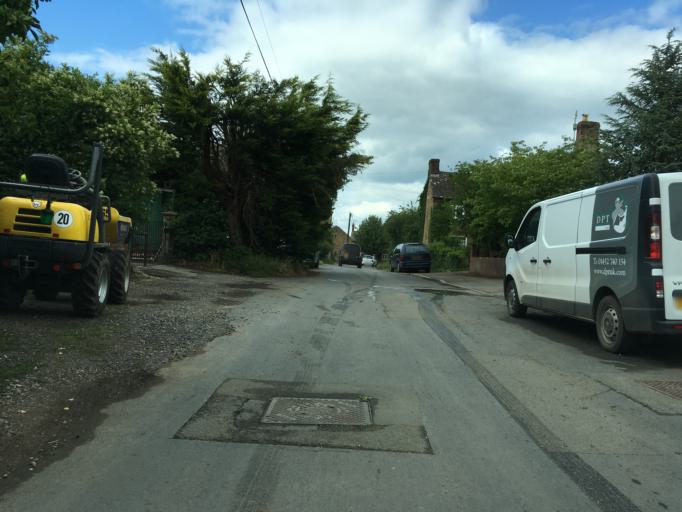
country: GB
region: England
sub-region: Gloucestershire
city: Cinderford
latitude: 51.7977
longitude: -2.4240
